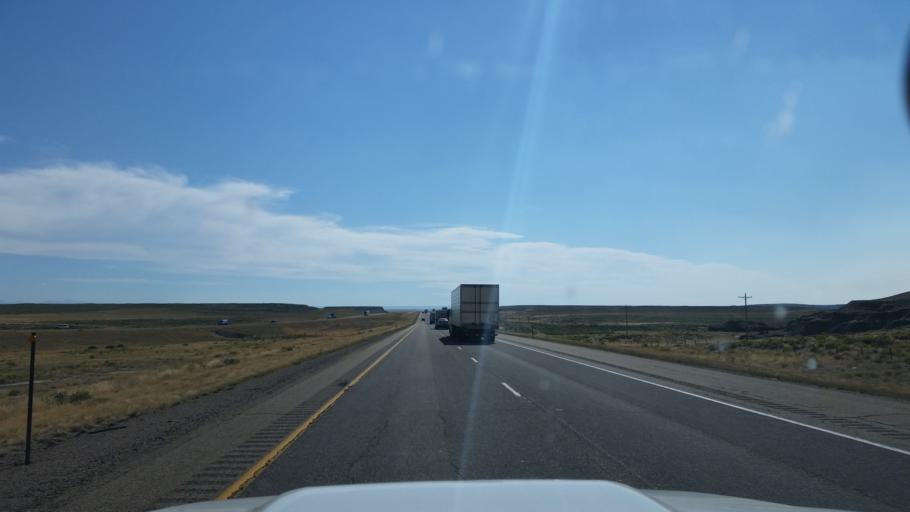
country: US
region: Wyoming
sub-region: Uinta County
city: Lyman
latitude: 41.4096
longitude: -110.1514
